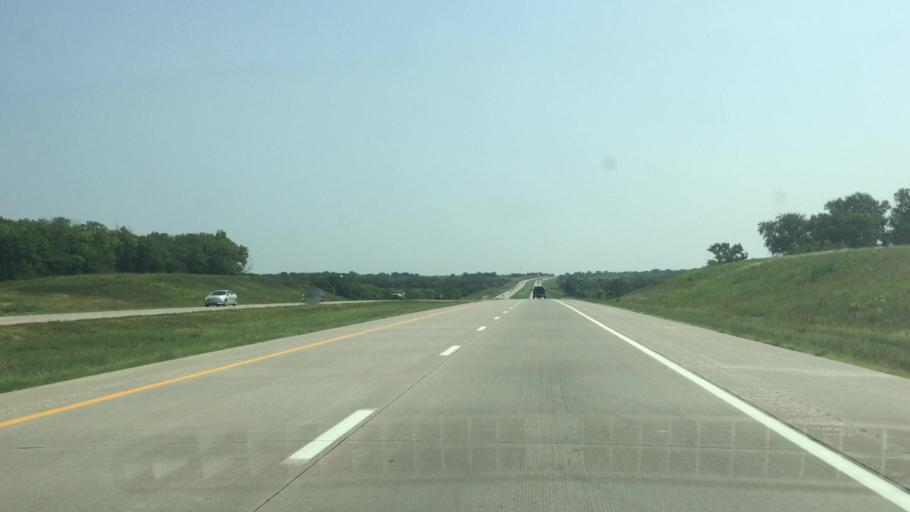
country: US
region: Kansas
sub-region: Osage County
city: Lyndon
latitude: 38.4396
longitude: -95.6853
